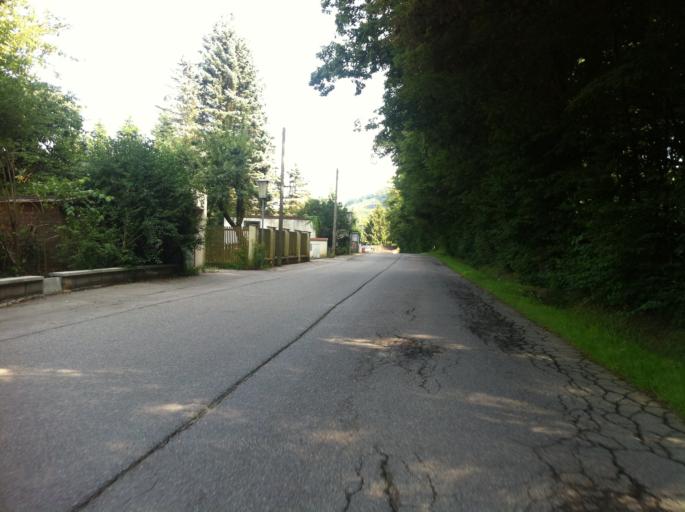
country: AT
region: Lower Austria
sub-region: Politischer Bezirk Wien-Umgebung
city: Purkersdorf
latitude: 48.1852
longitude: 16.1748
